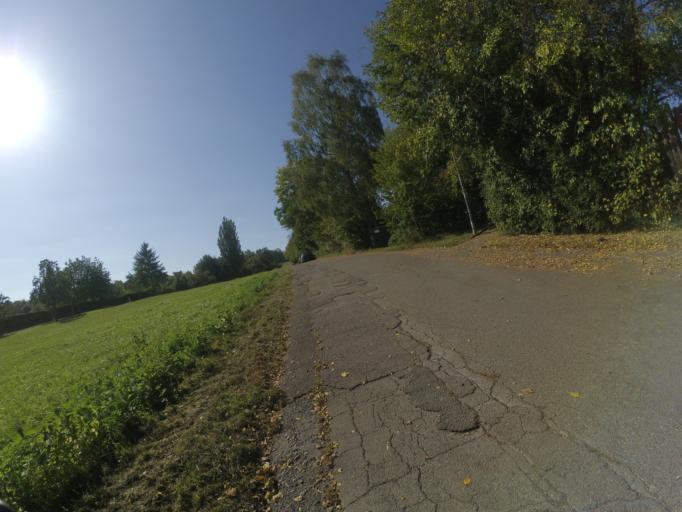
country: DE
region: Baden-Wuerttemberg
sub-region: Tuebingen Region
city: Ulm
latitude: 48.3880
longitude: 9.9517
